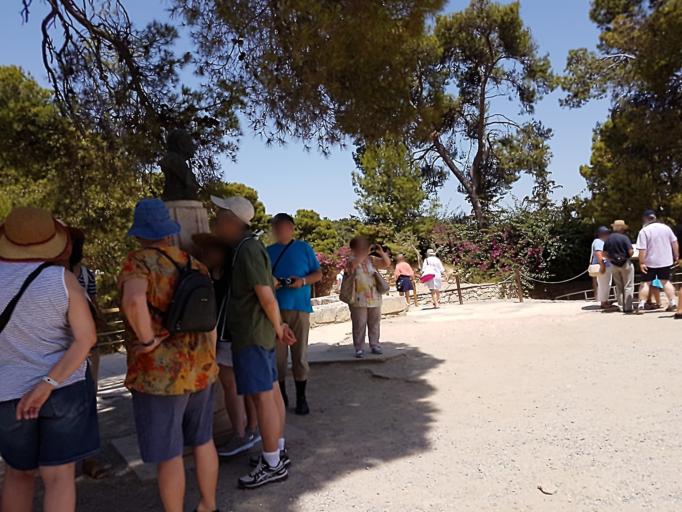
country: GR
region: Crete
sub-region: Nomos Irakleiou
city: Skalanion
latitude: 35.2978
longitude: 25.1622
